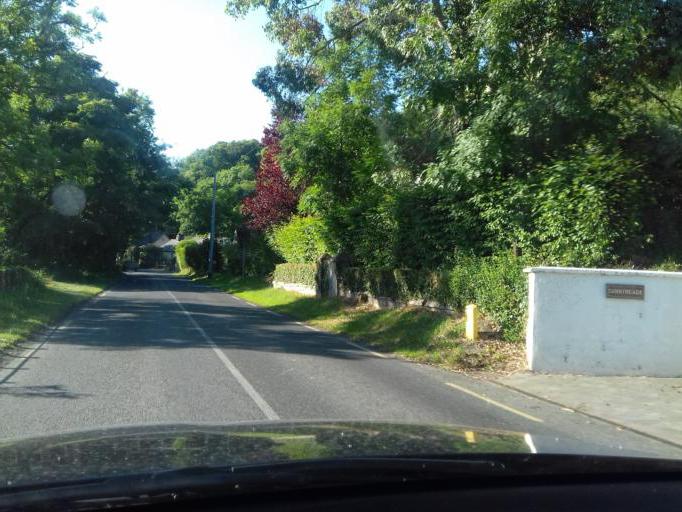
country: IE
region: Leinster
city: Hartstown
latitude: 53.3651
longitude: -6.4097
